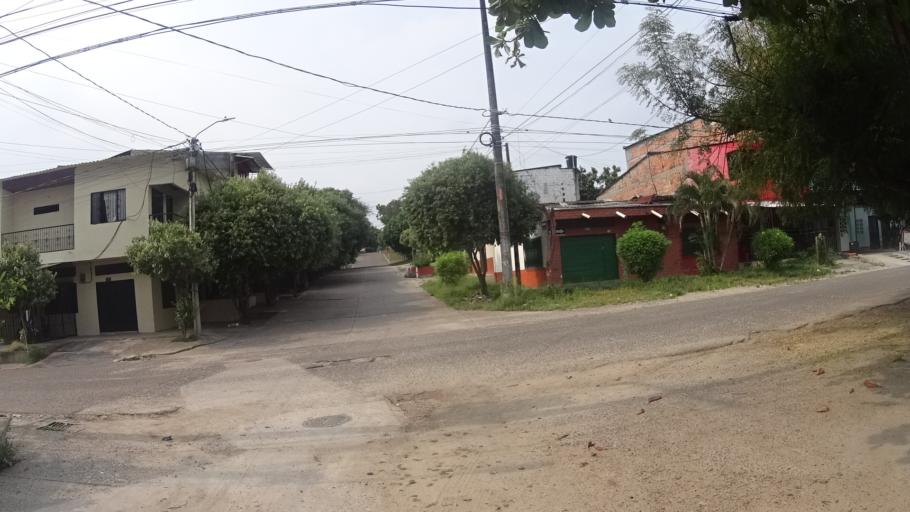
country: CO
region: Caldas
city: La Dorada
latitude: 5.4551
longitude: -74.6684
